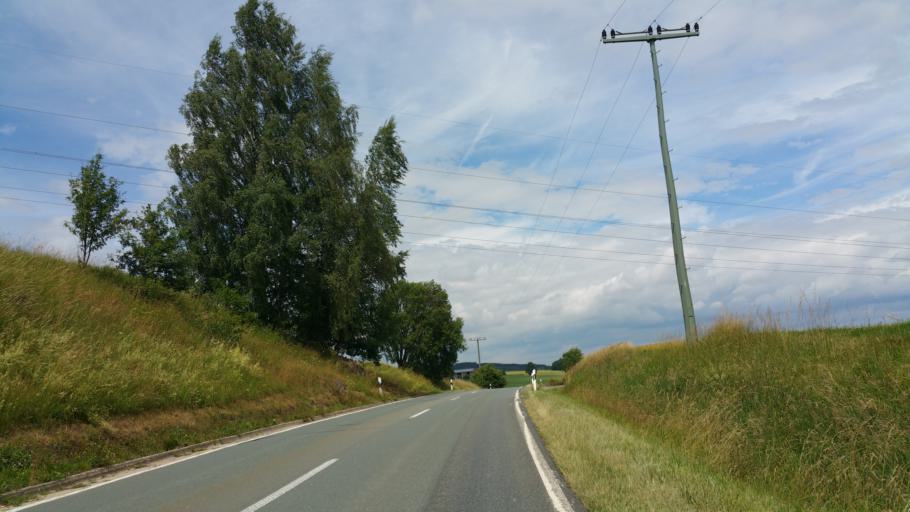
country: DE
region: Bavaria
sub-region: Upper Franconia
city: Schwarzenbach an der Saale
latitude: 50.2278
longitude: 11.9090
